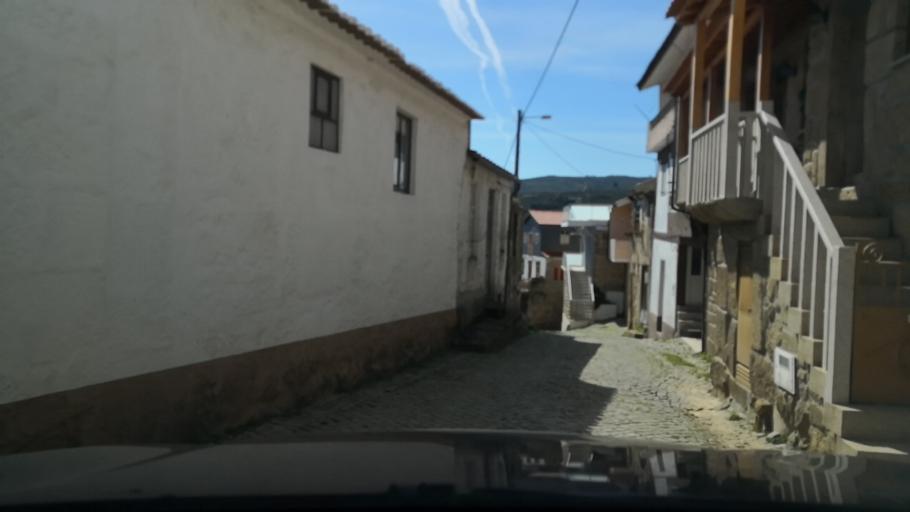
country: PT
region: Vila Real
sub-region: Sabrosa
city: Sabrosa
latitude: 41.3352
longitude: -7.5897
